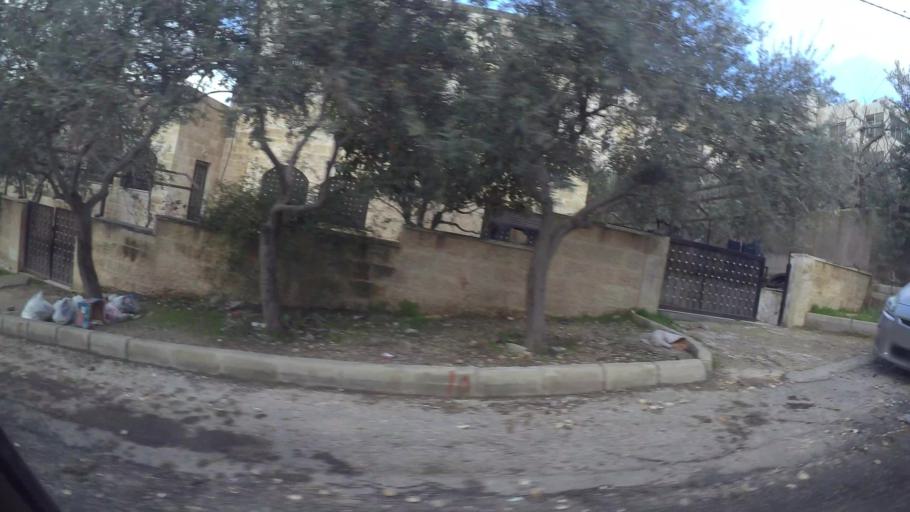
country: JO
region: Amman
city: Al Jubayhah
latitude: 32.0496
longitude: 35.8899
